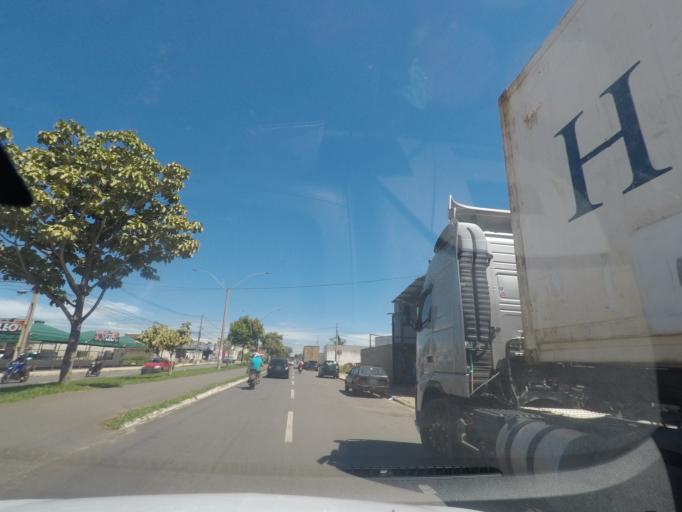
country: BR
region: Goias
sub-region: Aparecida De Goiania
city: Aparecida de Goiania
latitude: -16.7726
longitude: -49.3402
